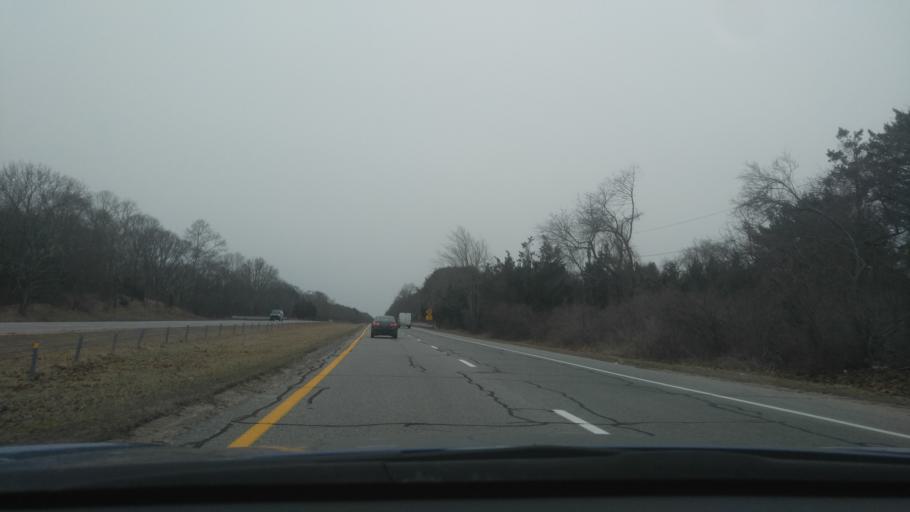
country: US
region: Rhode Island
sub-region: Washington County
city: Wakefield-Peacedale
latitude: 41.4247
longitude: -71.5242
